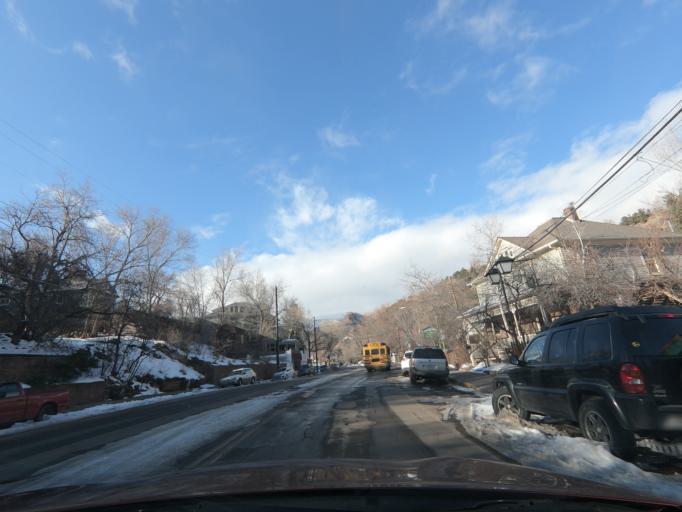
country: US
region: Colorado
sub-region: El Paso County
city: Manitou Springs
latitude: 38.8609
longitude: -104.9210
